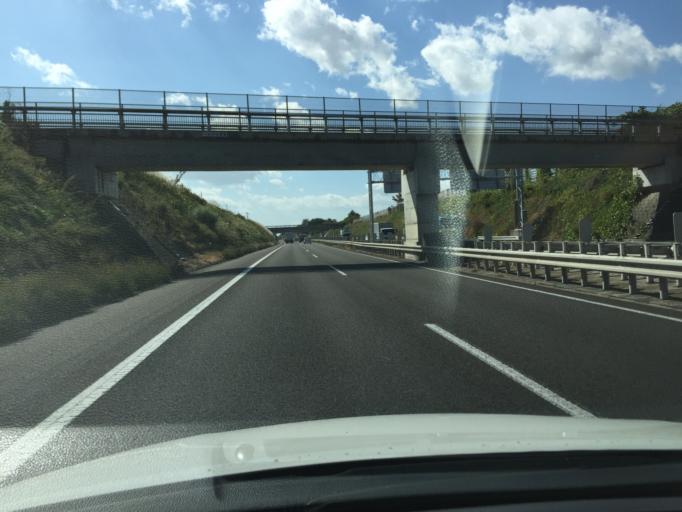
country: JP
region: Fukushima
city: Koriyama
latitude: 37.4599
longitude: 140.3587
